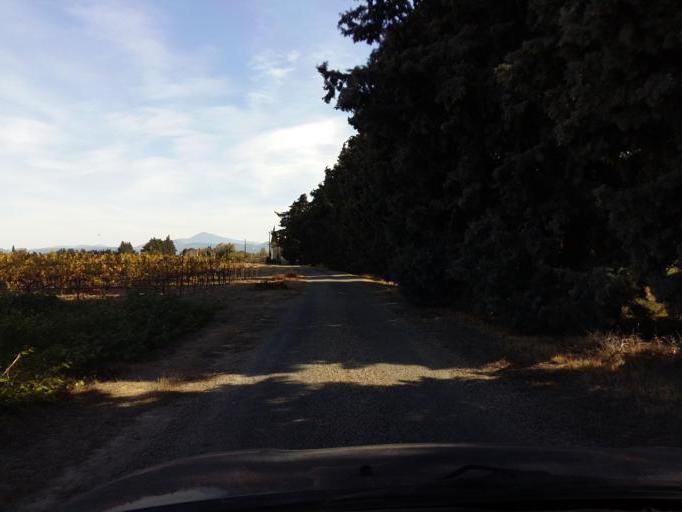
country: FR
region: Provence-Alpes-Cote d'Azur
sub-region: Departement du Vaucluse
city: Serignan-du-Comtat
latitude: 44.1706
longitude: 4.8371
